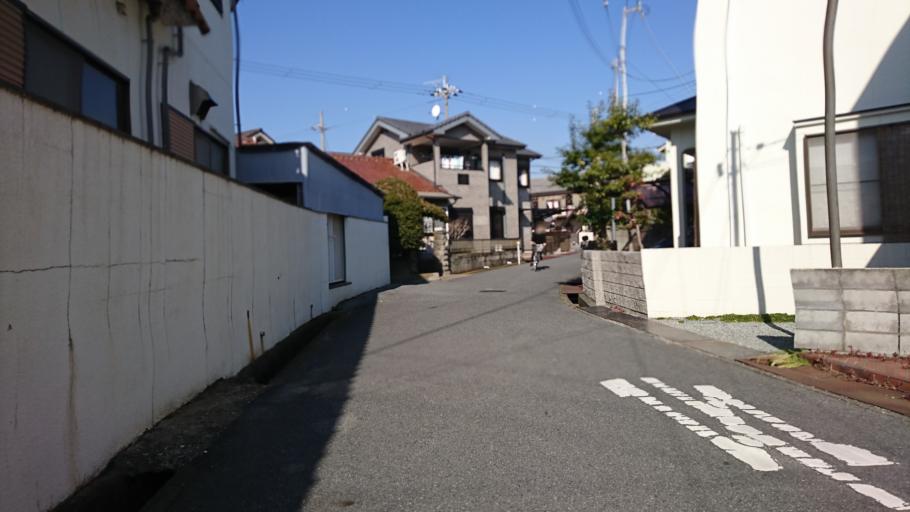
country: JP
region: Hyogo
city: Kakogawacho-honmachi
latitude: 34.7399
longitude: 134.8681
